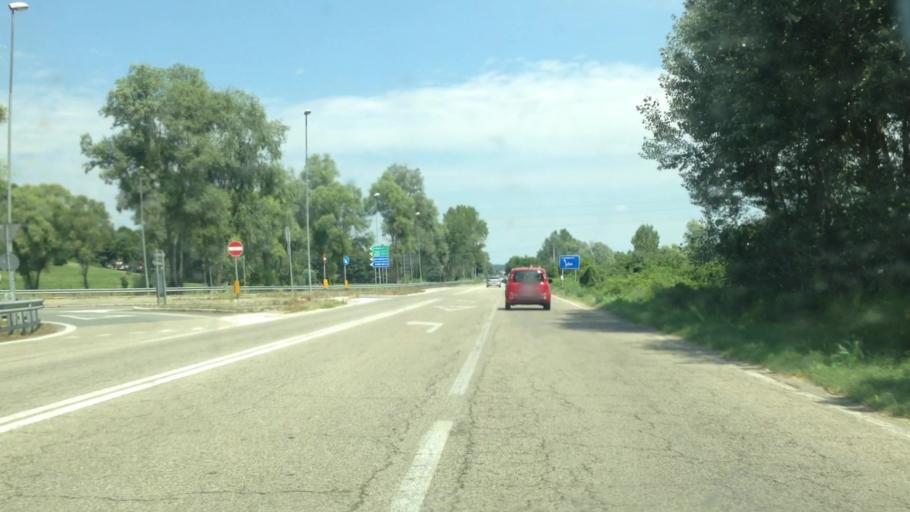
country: IT
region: Piedmont
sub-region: Provincia di Asti
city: Asti
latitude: 44.9247
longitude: 8.2261
